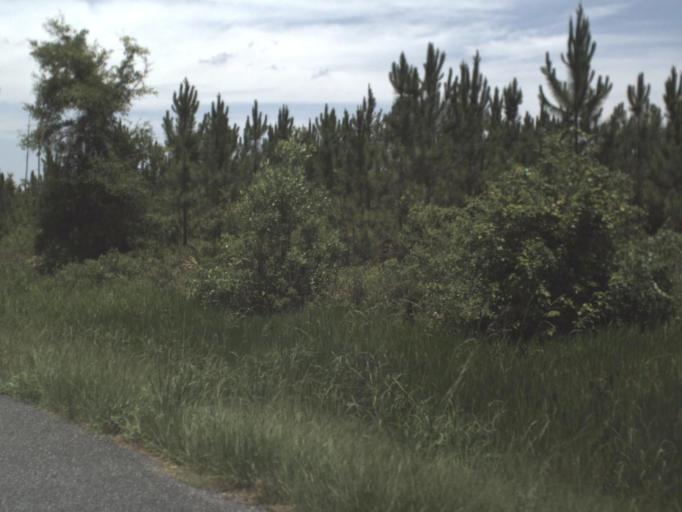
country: US
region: Florida
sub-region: Lafayette County
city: Mayo
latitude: 30.0104
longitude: -83.1928
